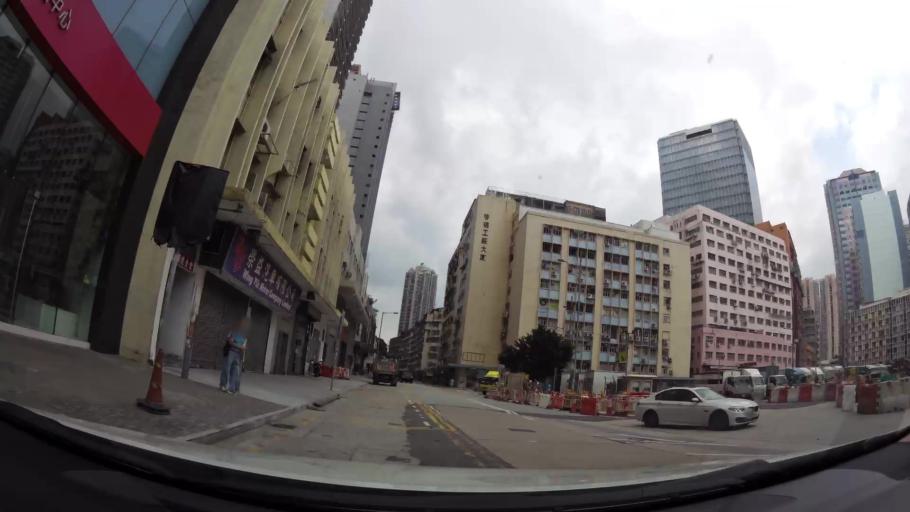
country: HK
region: Wong Tai Sin
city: Wong Tai Sin
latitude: 22.3349
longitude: 114.1995
